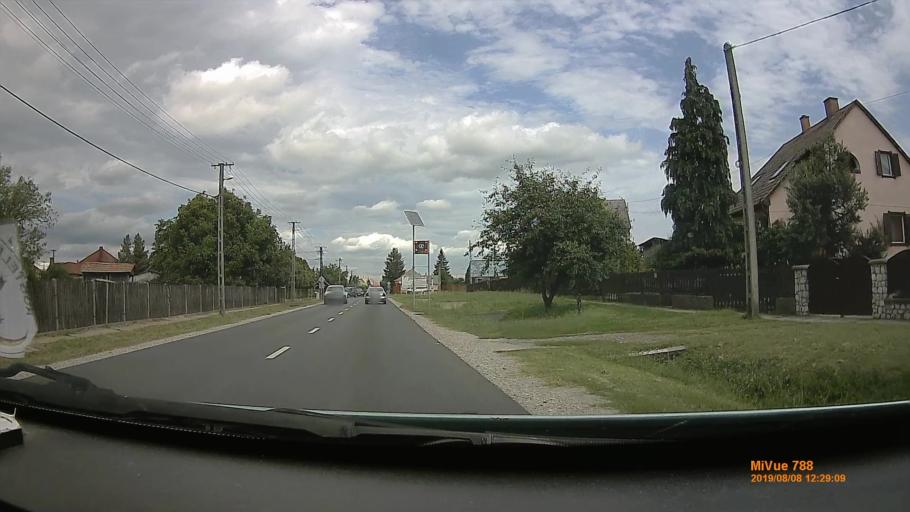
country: HU
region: Szabolcs-Szatmar-Bereg
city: Nyirbator
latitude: 47.8336
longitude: 22.1172
